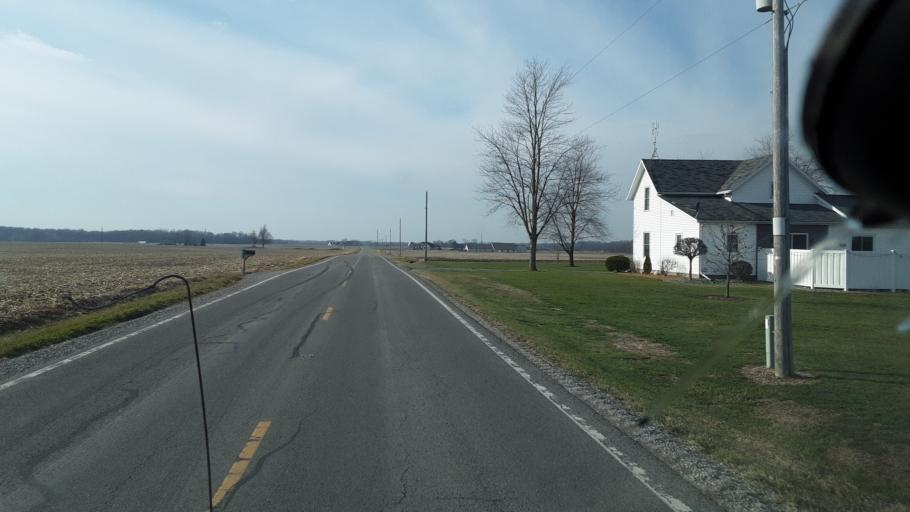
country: US
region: Ohio
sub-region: Williams County
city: Edgerton
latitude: 41.3827
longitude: -84.7591
